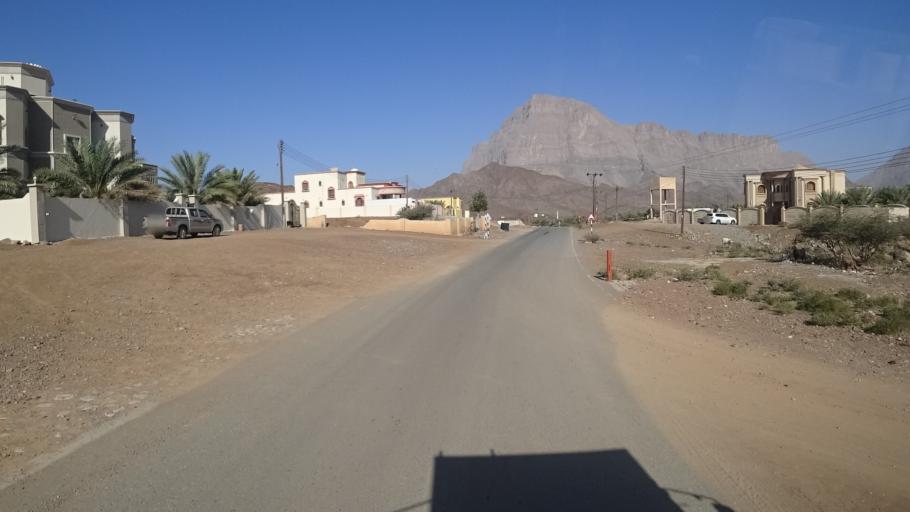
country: OM
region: Muhafazat ad Dakhiliyah
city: Bahla'
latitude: 23.2273
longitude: 57.0476
